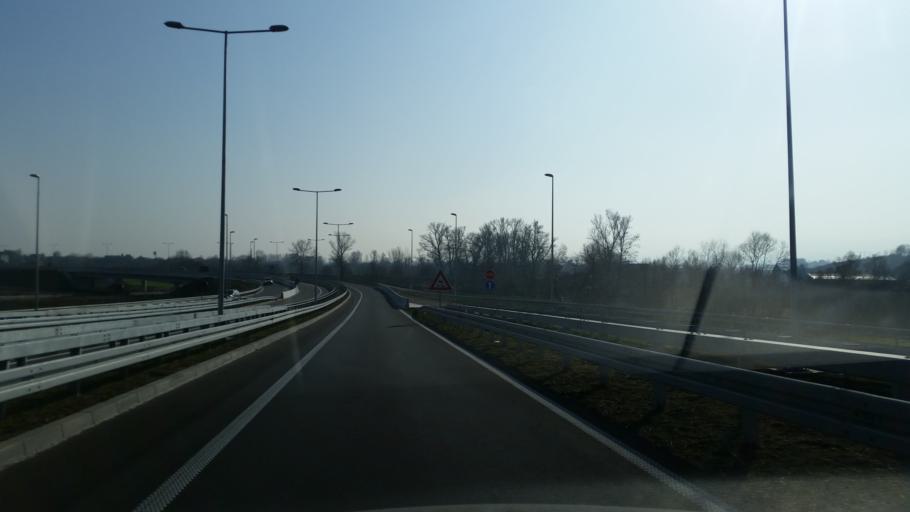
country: RS
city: Prislonica
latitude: 43.9192
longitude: 20.3948
